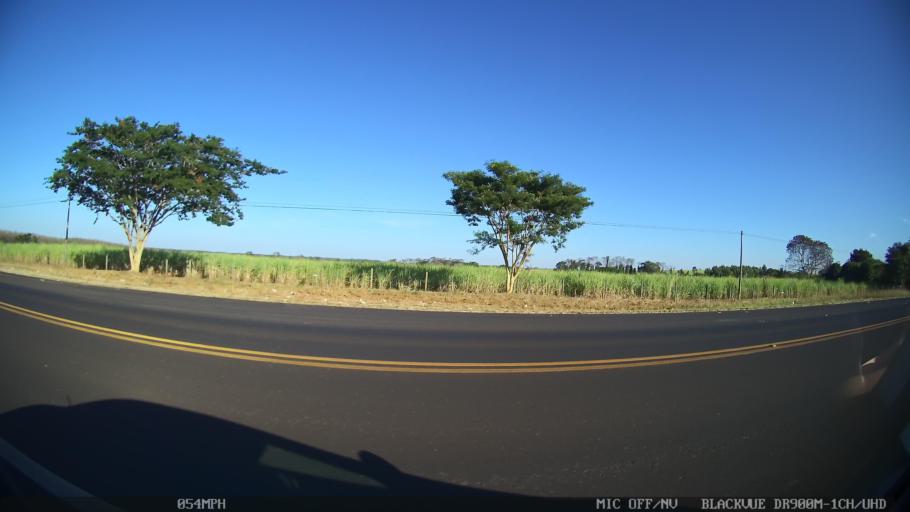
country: BR
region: Sao Paulo
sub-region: Olimpia
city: Olimpia
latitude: -20.7136
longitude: -48.9877
